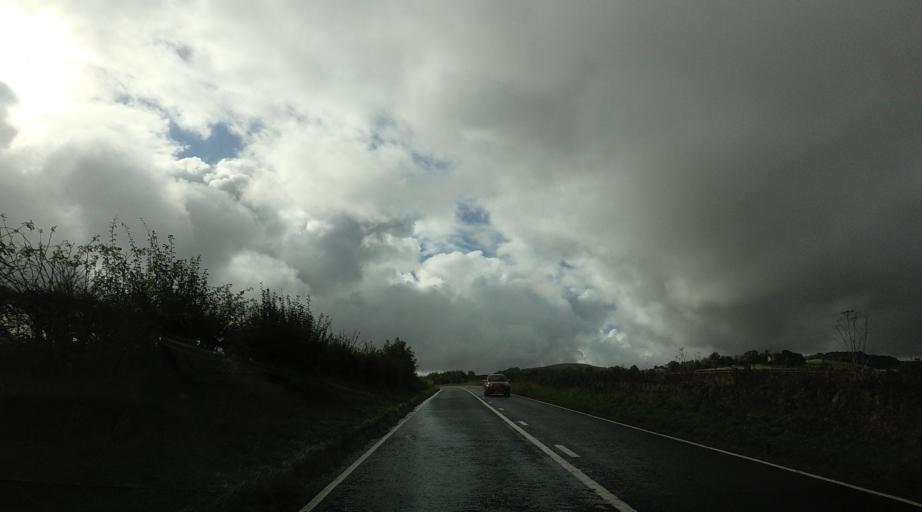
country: GB
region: Scotland
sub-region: Fife
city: Balmullo
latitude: 56.3634
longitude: -2.9377
